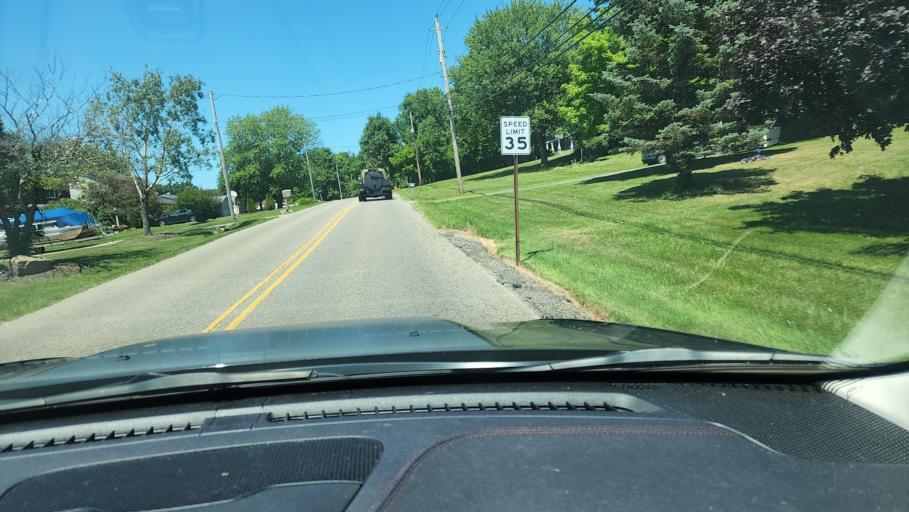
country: US
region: Ohio
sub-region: Mahoning County
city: Austintown
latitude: 41.0792
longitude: -80.7893
